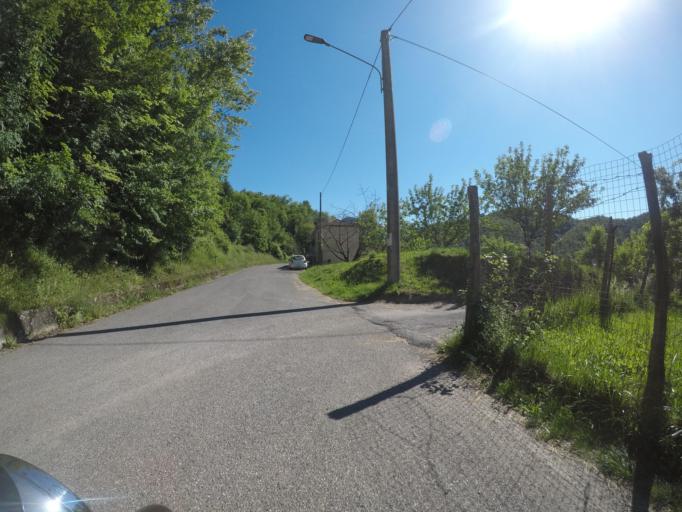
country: IT
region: Tuscany
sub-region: Provincia di Massa-Carrara
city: Fosdinovo
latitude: 44.1523
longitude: 10.1026
